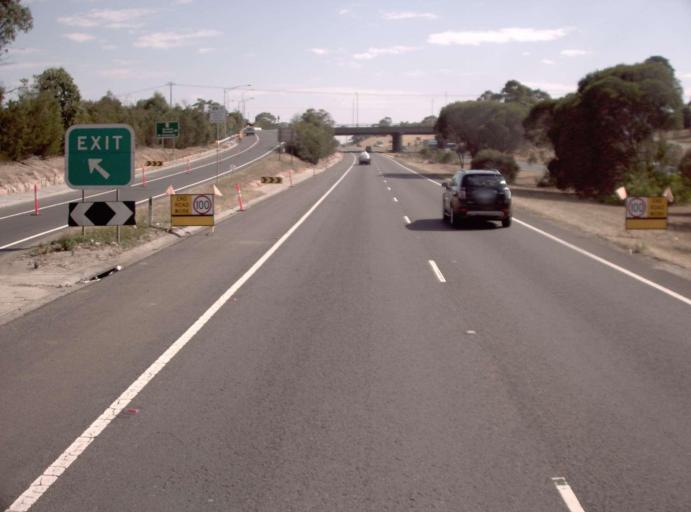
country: AU
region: Victoria
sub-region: Casey
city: Eumemmerring
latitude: -38.0061
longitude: 145.2513
